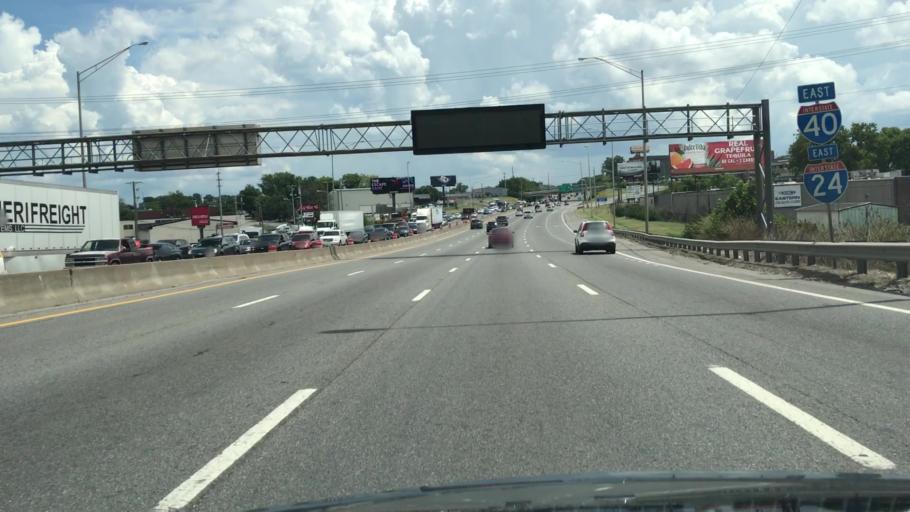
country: US
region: Tennessee
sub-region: Davidson County
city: Nashville
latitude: 36.1503
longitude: -86.7491
